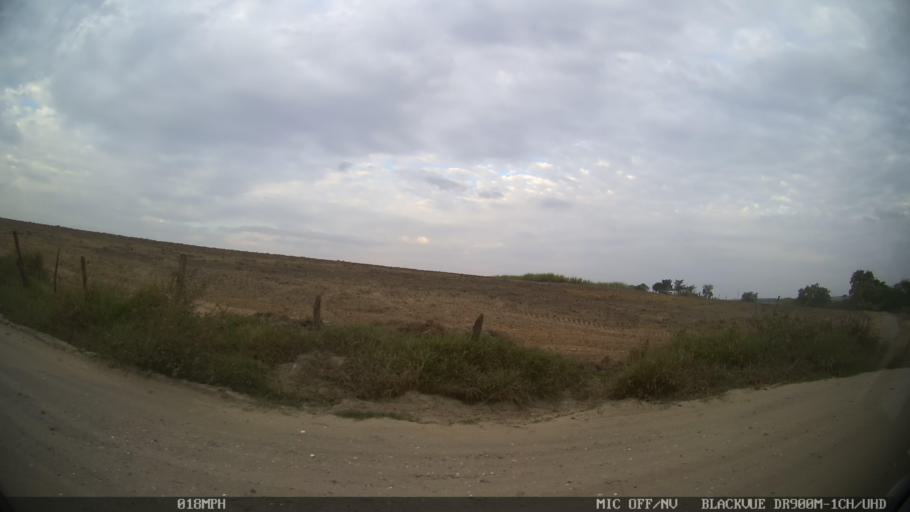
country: BR
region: Sao Paulo
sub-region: Santa Barbara D'Oeste
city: Santa Barbara d'Oeste
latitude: -22.6870
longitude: -47.3883
